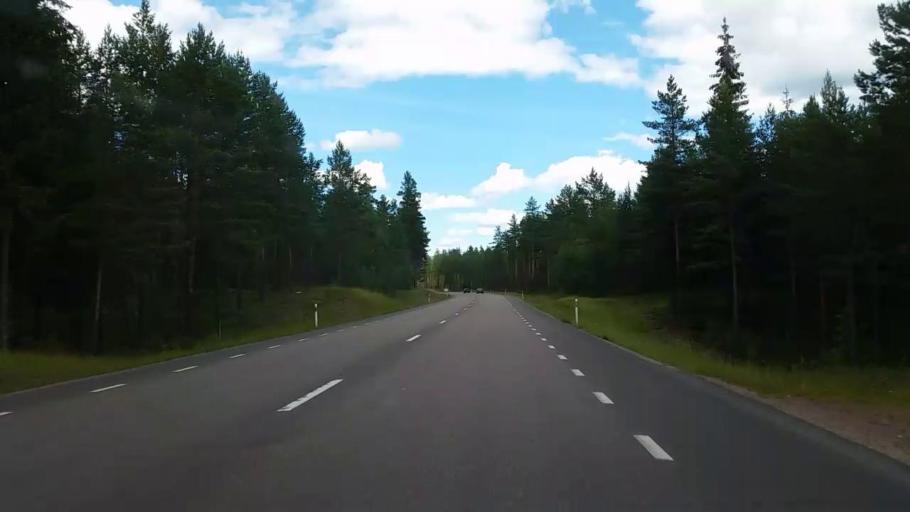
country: SE
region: Dalarna
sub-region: Leksand Municipality
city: Smedby
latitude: 60.6537
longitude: 15.0747
